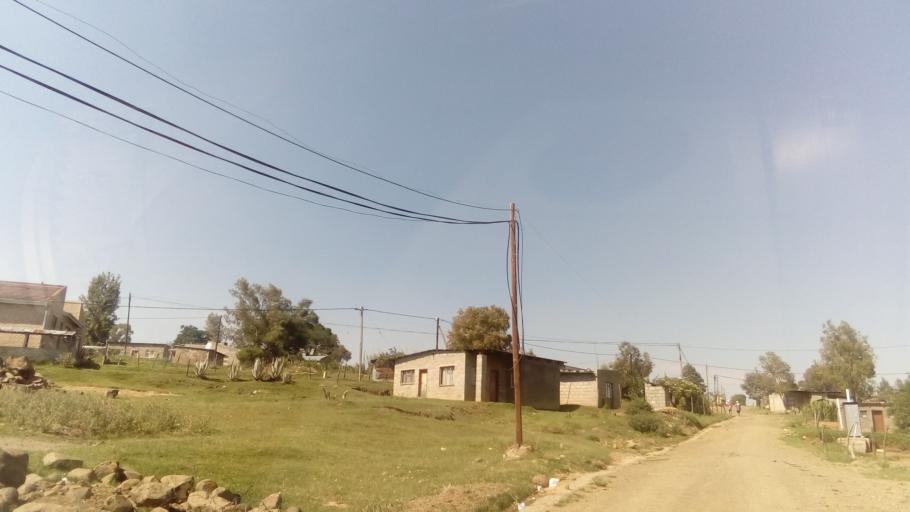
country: LS
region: Berea
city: Teyateyaneng
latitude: -29.1456
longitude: 27.7559
